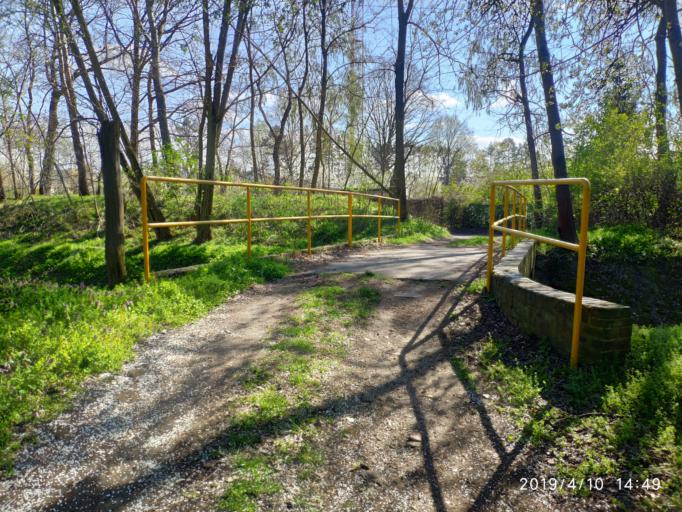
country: PL
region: Lubusz
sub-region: Zielona Gora
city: Zielona Gora
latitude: 51.9485
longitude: 15.4723
